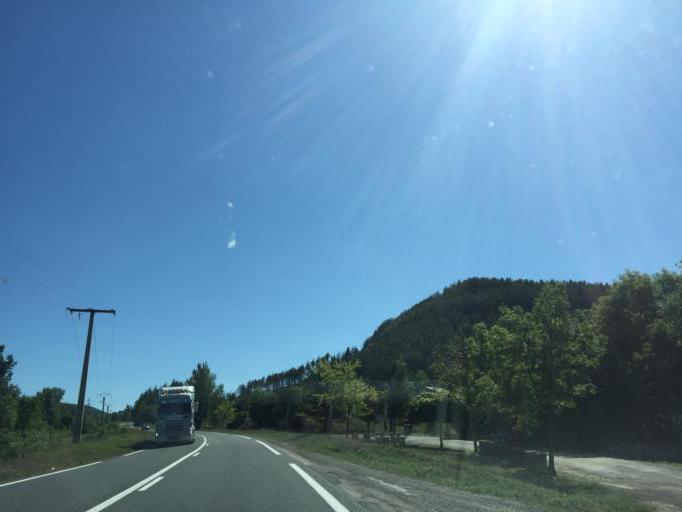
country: FR
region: Midi-Pyrenees
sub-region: Departement de l'Aveyron
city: Saint-Affrique
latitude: 43.9838
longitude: 2.9663
